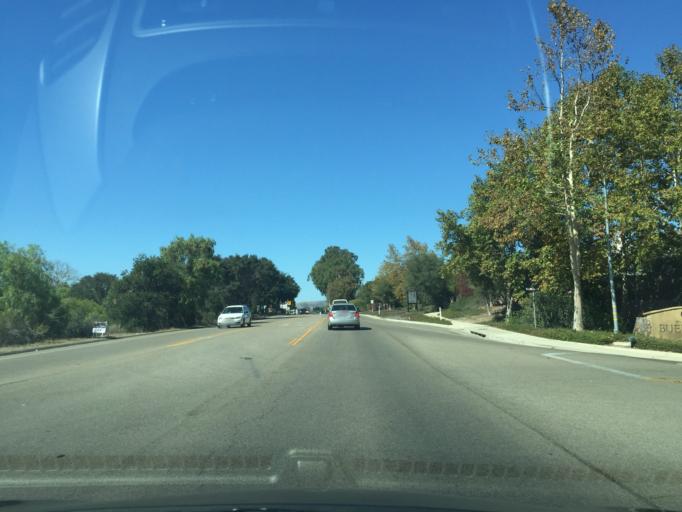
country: US
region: California
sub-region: Santa Barbara County
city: Buellton
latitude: 34.6079
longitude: -120.1791
